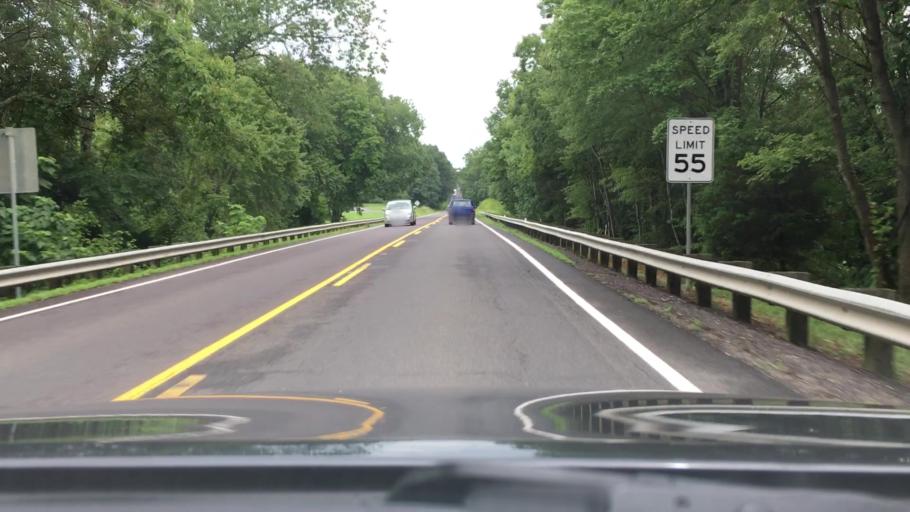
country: US
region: Virginia
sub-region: Orange County
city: Orange
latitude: 38.2692
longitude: -77.9422
